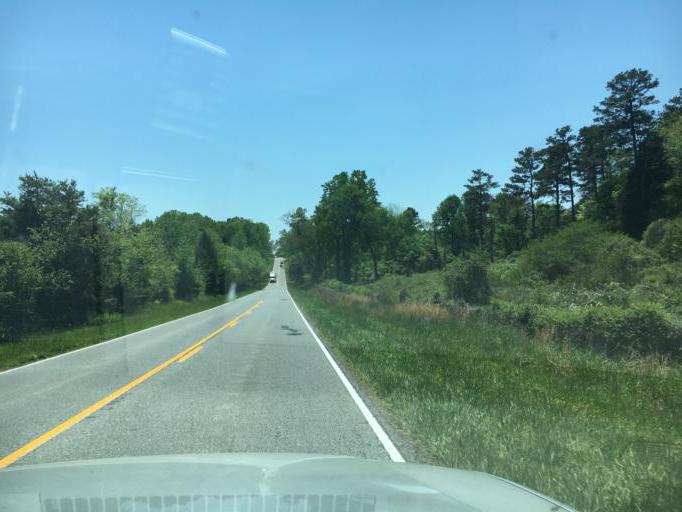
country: US
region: South Carolina
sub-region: Cherokee County
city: Blacksburg
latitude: 35.1454
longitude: -81.5755
